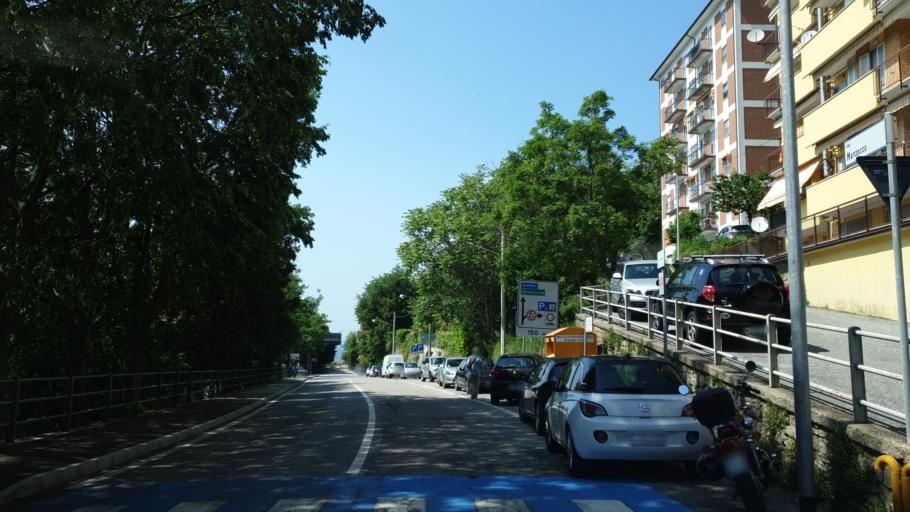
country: SM
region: San Marino
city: San Marino
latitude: 43.9333
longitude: 12.4463
